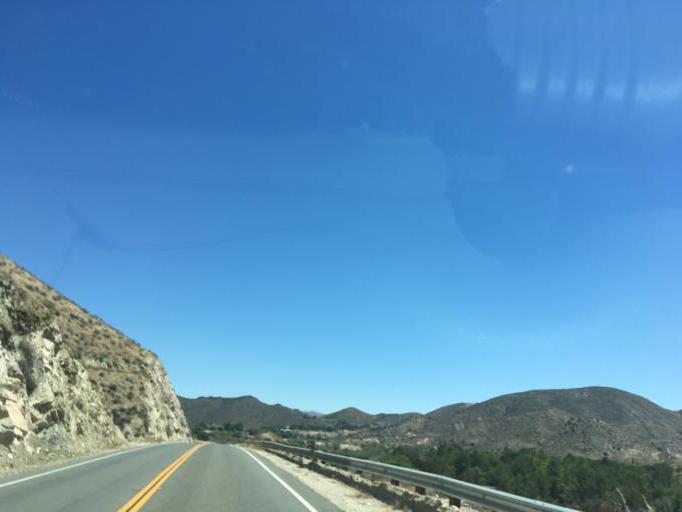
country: US
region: California
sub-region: Los Angeles County
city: Acton
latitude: 34.4487
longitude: -118.2071
